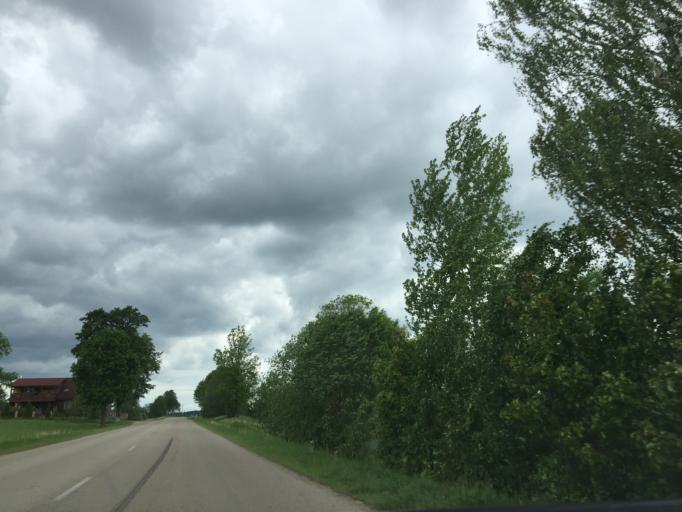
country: LV
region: Dagda
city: Dagda
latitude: 56.1050
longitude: 27.4969
